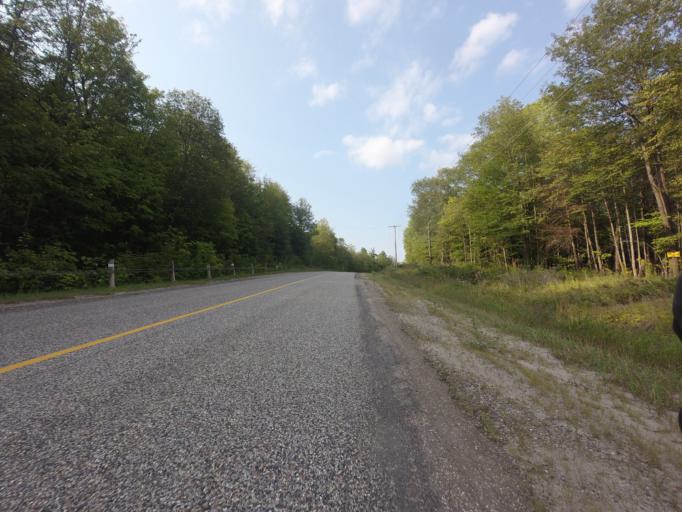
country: CA
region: Ontario
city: Perth
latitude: 44.9142
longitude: -76.6873
